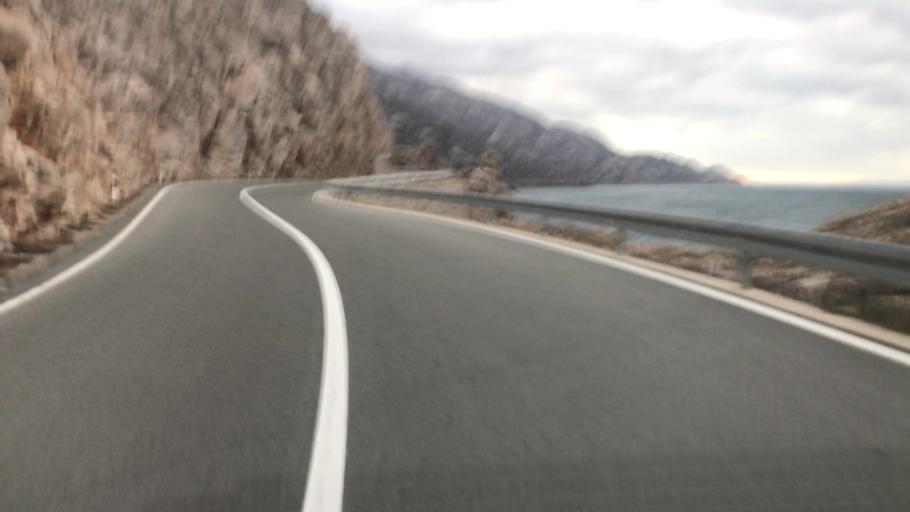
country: HR
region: Licko-Senjska
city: Karlobag
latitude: 44.5185
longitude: 15.0863
